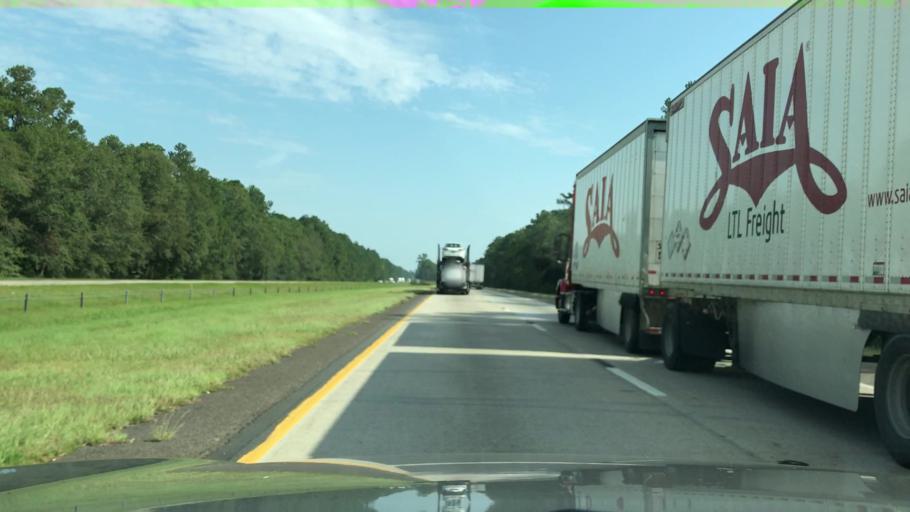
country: US
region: South Carolina
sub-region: Colleton County
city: Walterboro
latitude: 32.8403
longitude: -80.7399
